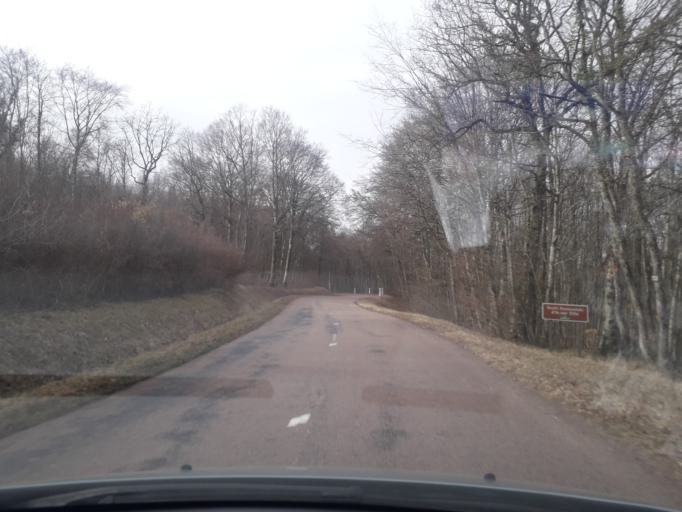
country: FR
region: Bourgogne
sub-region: Departement de la Cote-d'Or
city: Messigny-et-Vantoux
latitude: 47.4687
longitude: 4.9514
